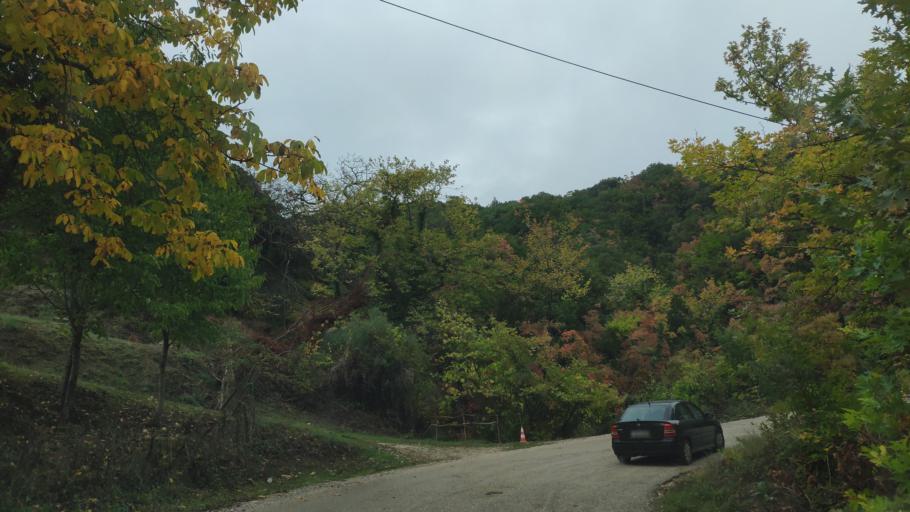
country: GR
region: Epirus
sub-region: Nomos Thesprotias
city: Paramythia
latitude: 39.4681
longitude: 20.6711
